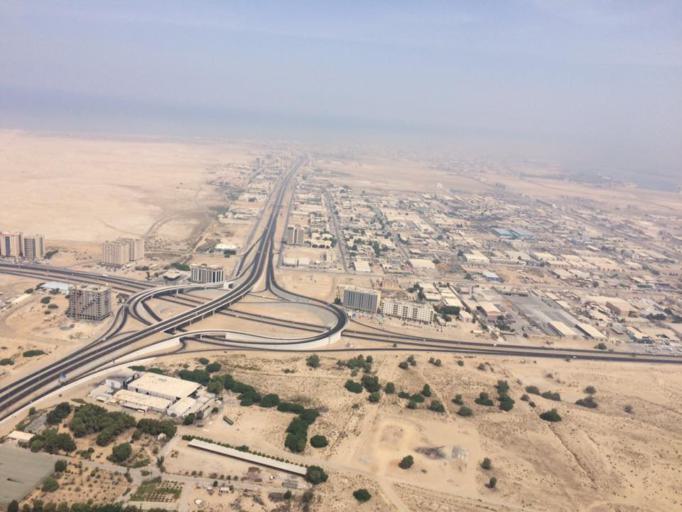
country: AE
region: Umm al Qaywayn
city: Umm al Qaywayn
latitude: 25.4890
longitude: 55.5552
